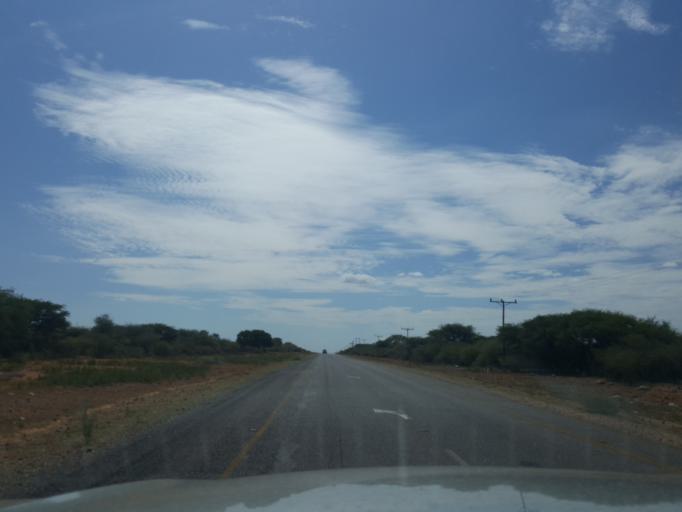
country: BW
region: Kweneng
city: Letlhakeng
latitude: -24.1477
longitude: 25.1526
